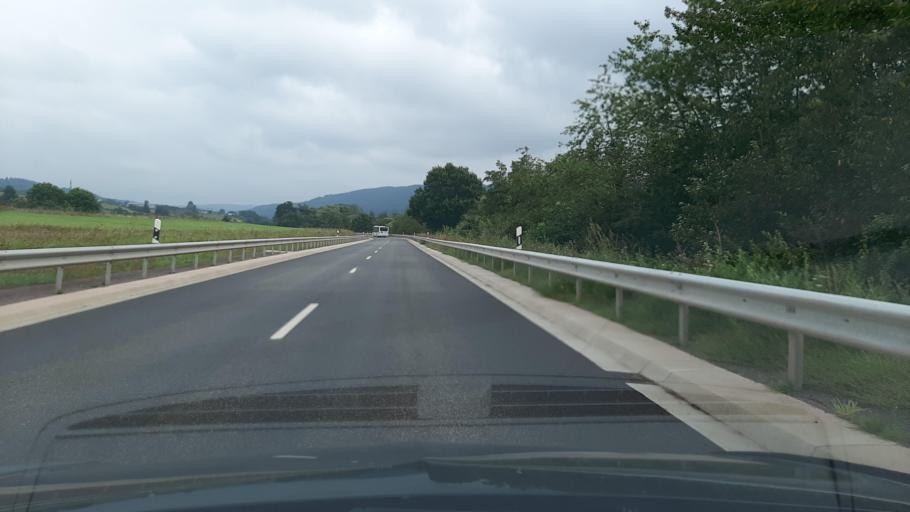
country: DE
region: Rheinland-Pfalz
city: Kinderbeuern
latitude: 50.0095
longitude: 7.0395
